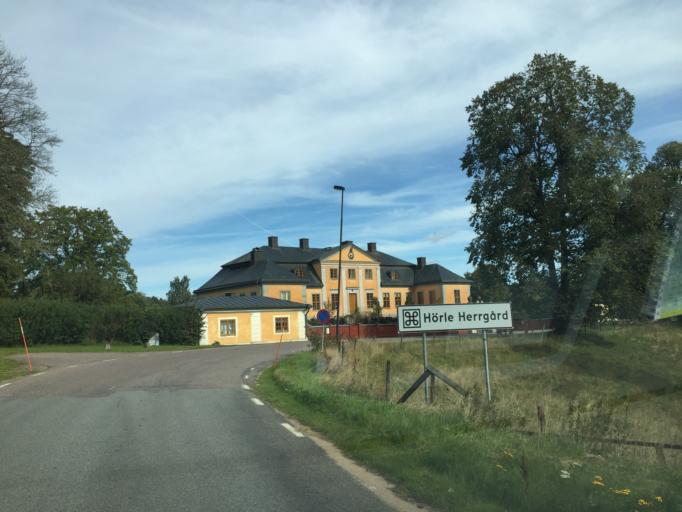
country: SE
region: Joenkoeping
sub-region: Varnamo Kommun
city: Varnamo
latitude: 57.2632
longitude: 14.0567
